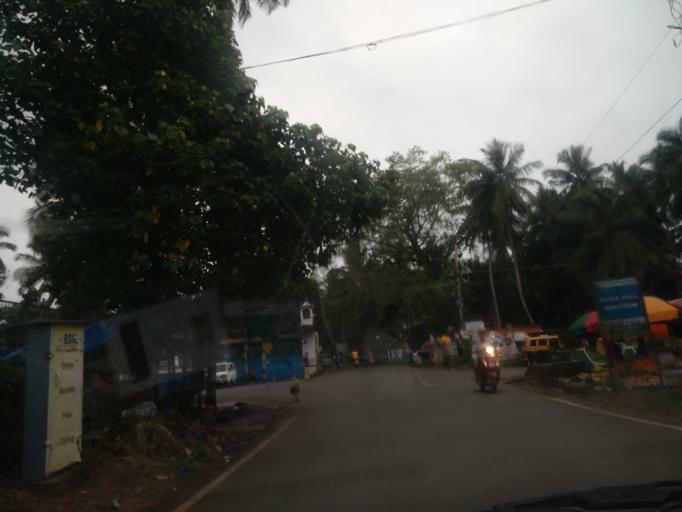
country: IN
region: Goa
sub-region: South Goa
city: Benaulim
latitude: 15.2612
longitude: 73.9302
